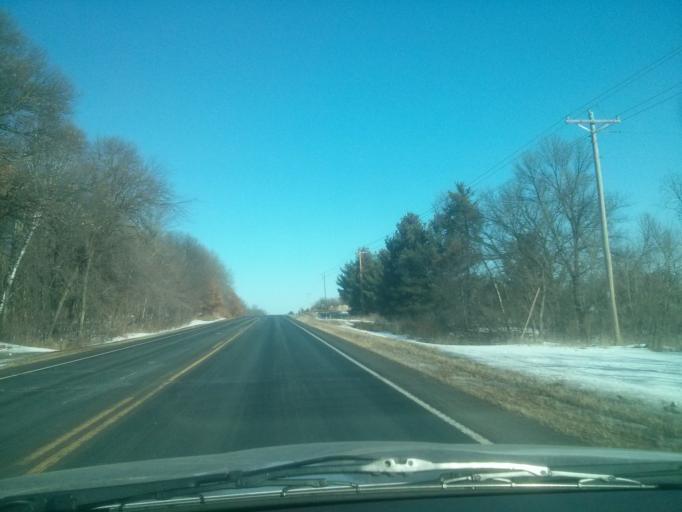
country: US
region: Minnesota
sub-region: Washington County
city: Stillwater
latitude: 45.0812
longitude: -92.7361
